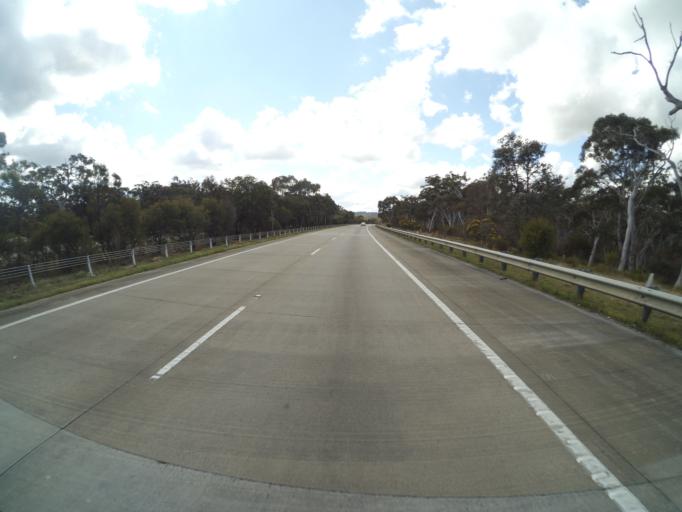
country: AU
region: New South Wales
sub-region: Wingecarribee
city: Moss Vale
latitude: -34.4788
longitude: 150.3173
